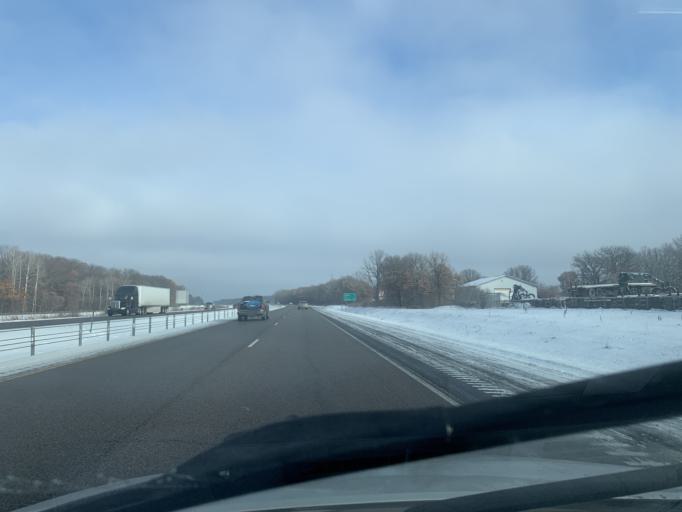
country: US
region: Minnesota
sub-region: Chisago County
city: Wyoming
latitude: 45.3467
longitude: -93.0010
